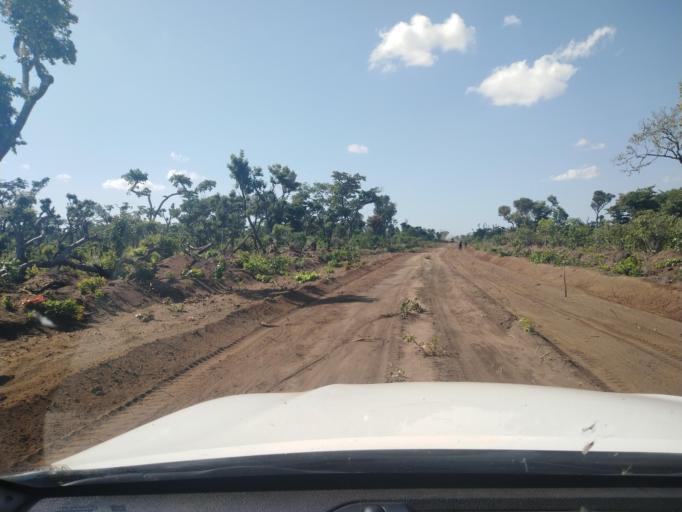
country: ZM
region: Northern
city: Chinsali
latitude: -11.0105
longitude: 31.7739
